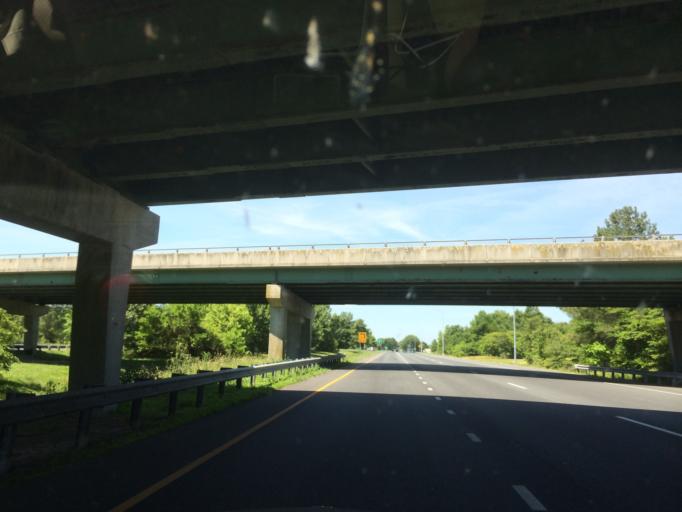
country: US
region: Maryland
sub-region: Wicomico County
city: Salisbury
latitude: 38.3698
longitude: -75.5372
